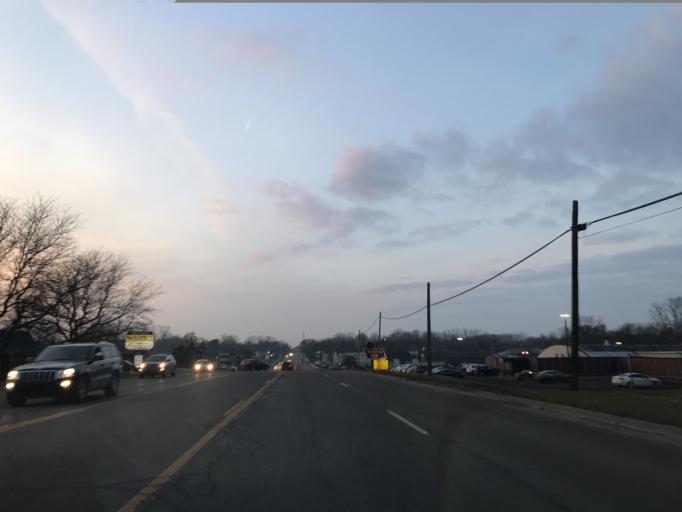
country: US
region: Michigan
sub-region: Livingston County
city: Brighton
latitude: 42.5221
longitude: -83.7643
